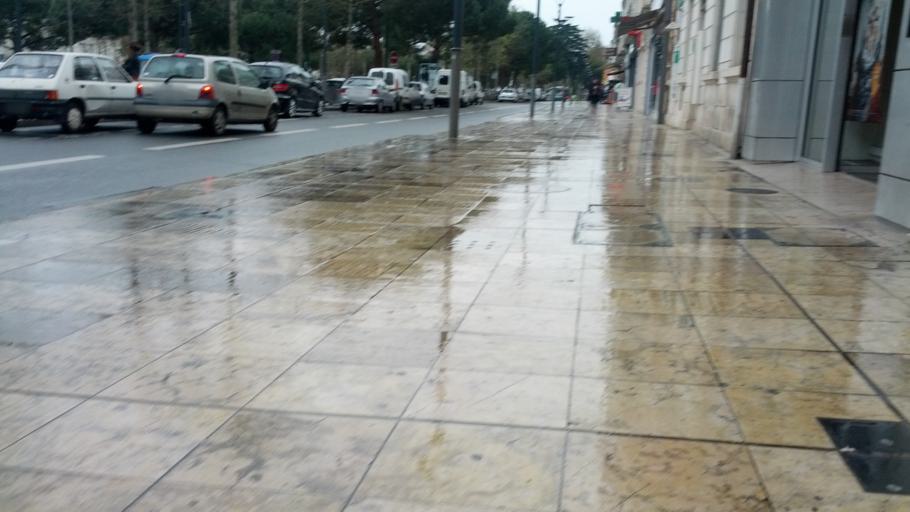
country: FR
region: Poitou-Charentes
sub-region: Departement de la Vienne
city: Chatellerault
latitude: 46.8172
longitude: 0.5452
